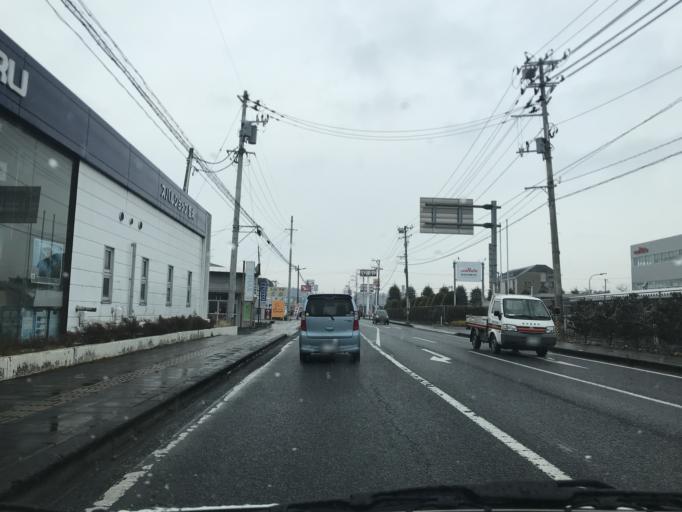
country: JP
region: Miyagi
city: Wakuya
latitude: 38.6874
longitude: 141.1872
